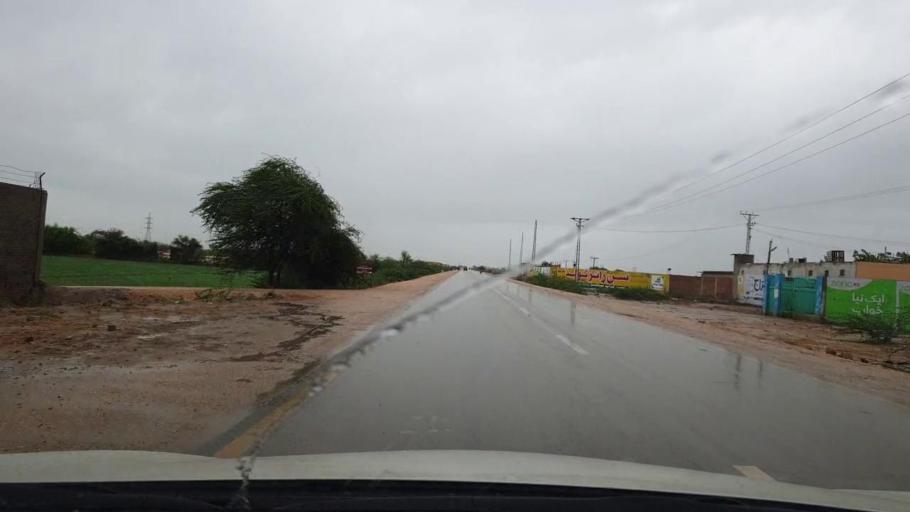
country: PK
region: Sindh
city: Kario
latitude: 24.6535
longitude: 68.5606
